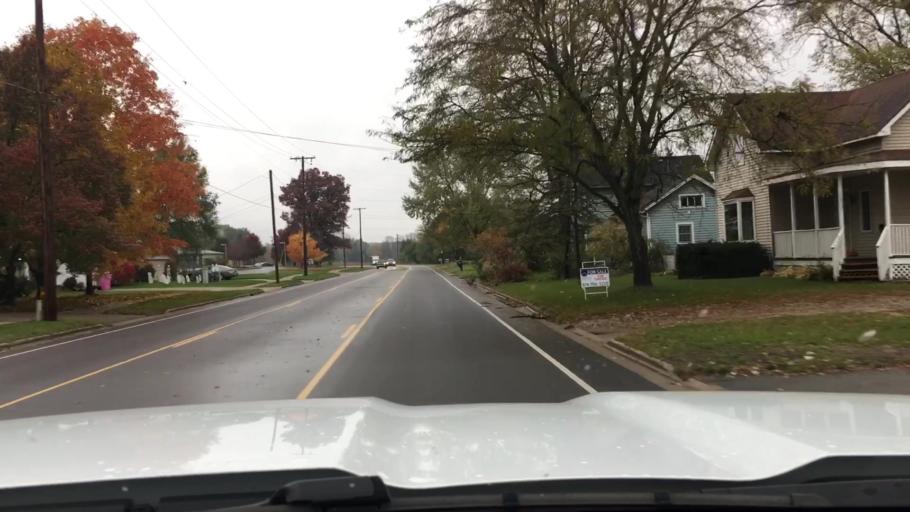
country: US
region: Michigan
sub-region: Kent County
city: Lowell
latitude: 42.9425
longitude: -85.3451
